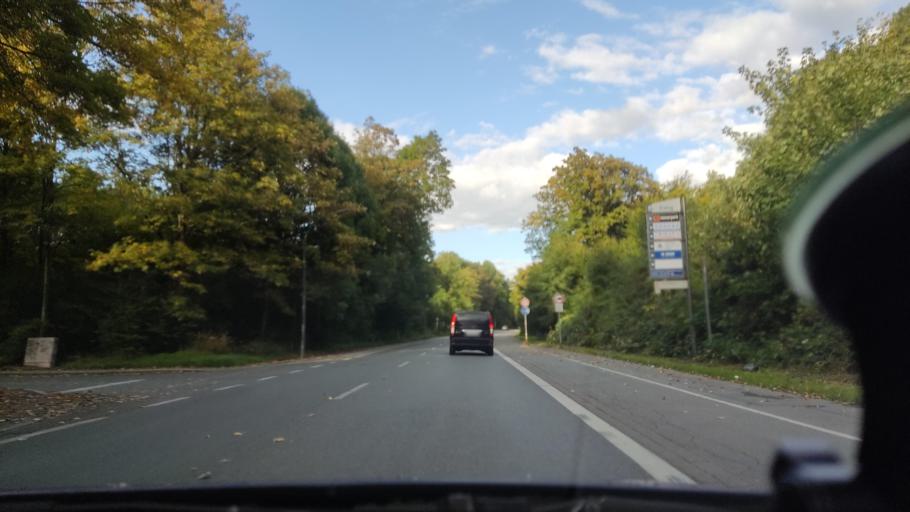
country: DE
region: North Rhine-Westphalia
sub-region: Regierungsbezirk Arnsberg
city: Dortmund
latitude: 51.5406
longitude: 7.4694
